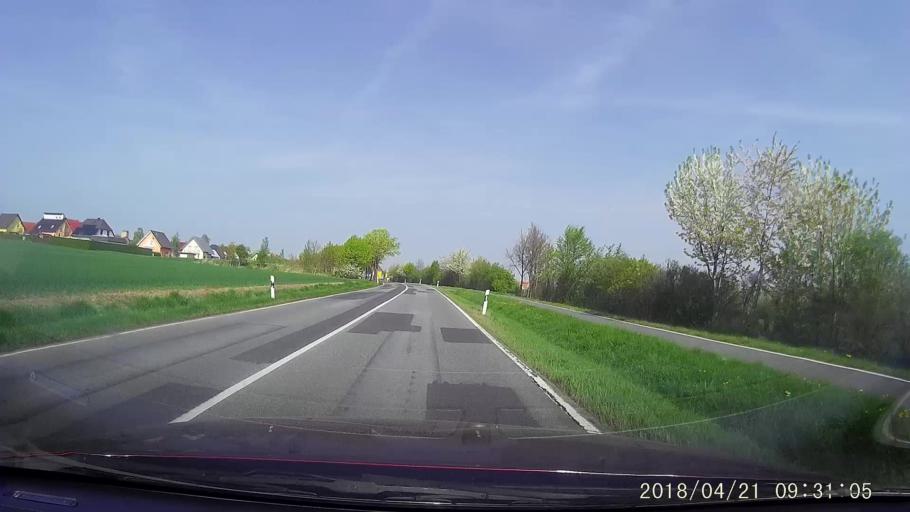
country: DE
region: Saxony
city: Radibor
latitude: 51.2082
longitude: 14.3998
